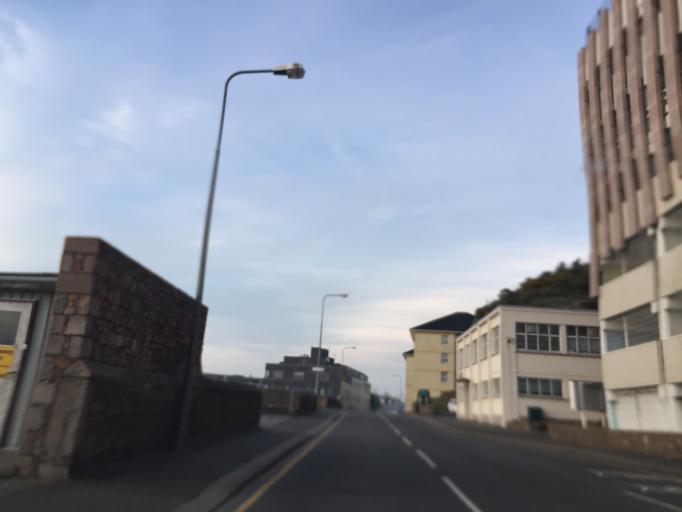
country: JE
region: St Helier
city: Saint Helier
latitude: 49.1805
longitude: -2.1080
